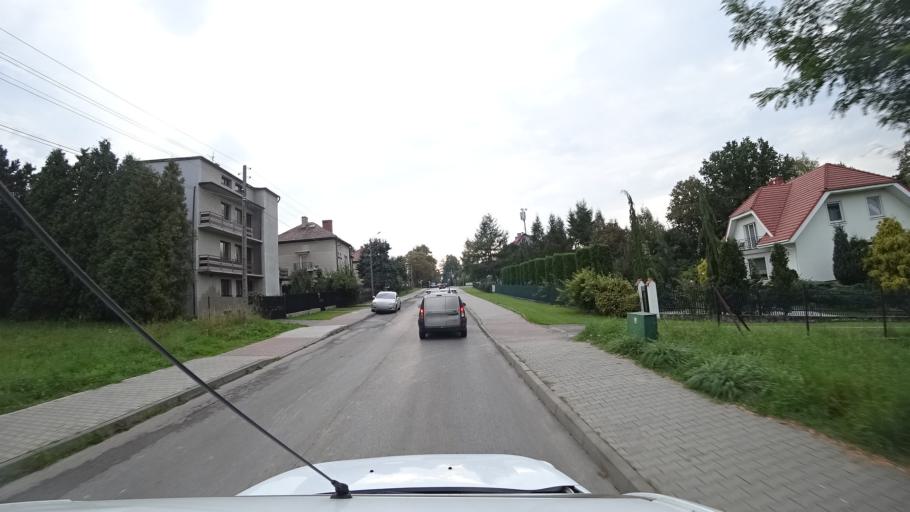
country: PL
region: Lesser Poland Voivodeship
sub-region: Powiat wadowicki
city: Kalwaria Zebrzydowska
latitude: 49.8688
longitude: 19.6833
